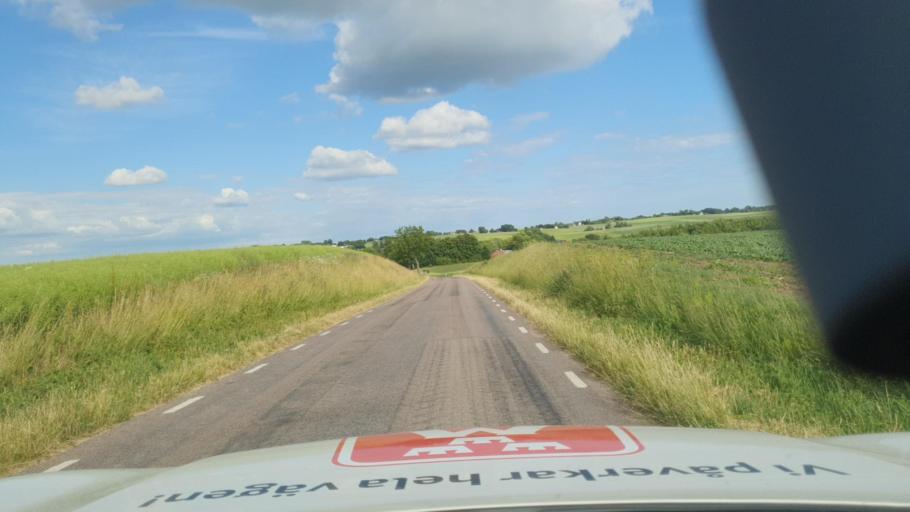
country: SE
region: Skane
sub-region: Skurups Kommun
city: Rydsgard
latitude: 55.4507
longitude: 13.5818
